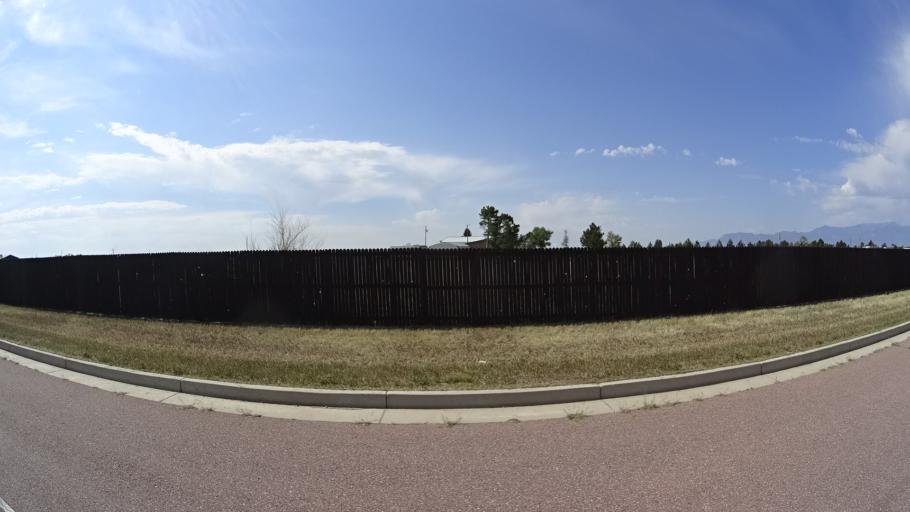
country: US
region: Colorado
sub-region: El Paso County
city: Cimarron Hills
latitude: 38.9265
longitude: -104.6726
